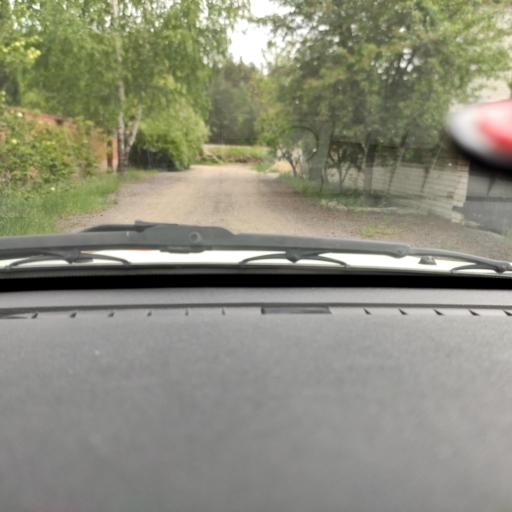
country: RU
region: Voronezj
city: Podgornoye
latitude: 51.7358
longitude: 39.1688
